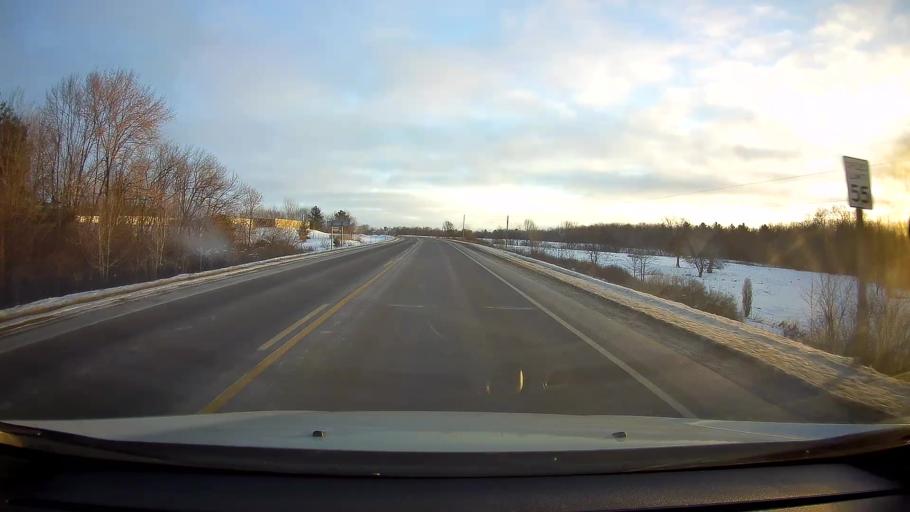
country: US
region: Wisconsin
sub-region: Polk County
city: Clear Lake
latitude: 45.2567
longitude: -92.2682
